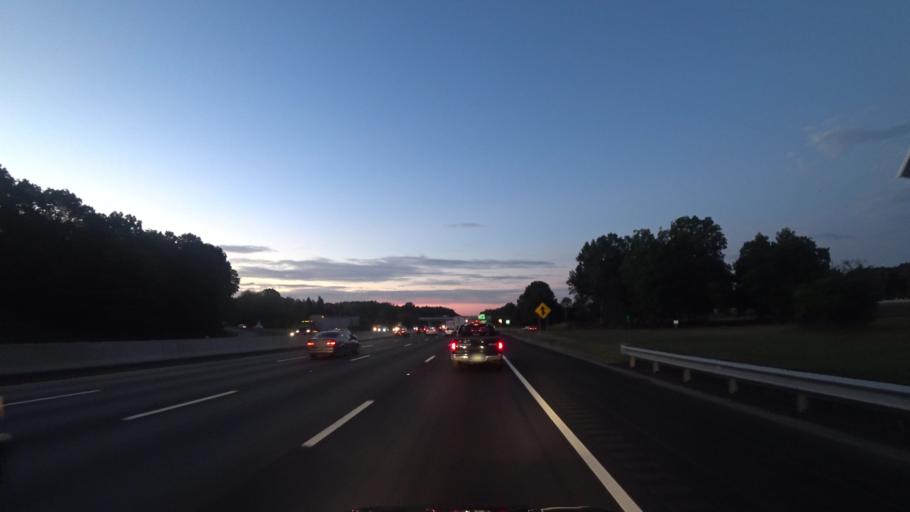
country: US
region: Massachusetts
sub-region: Middlesex County
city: Lexington
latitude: 42.4313
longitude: -71.2596
